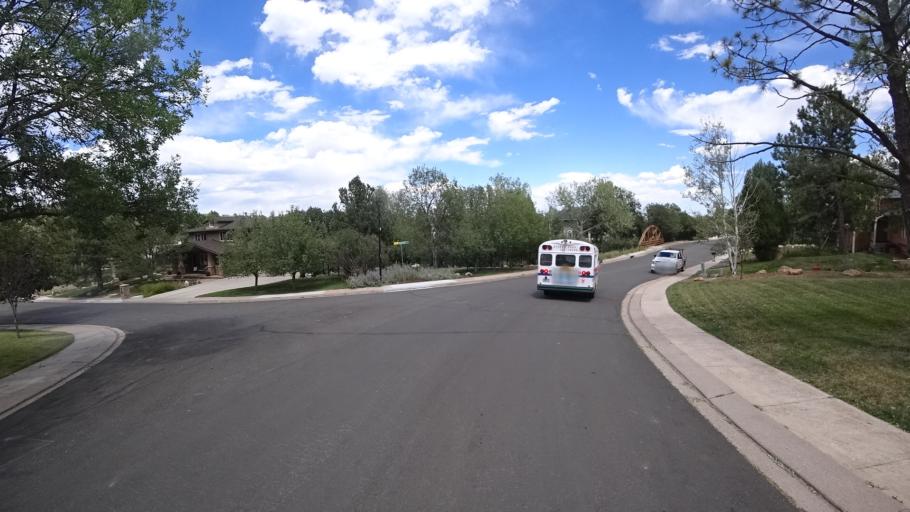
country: US
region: Colorado
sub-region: El Paso County
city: Stratmoor
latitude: 38.7760
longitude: -104.8344
